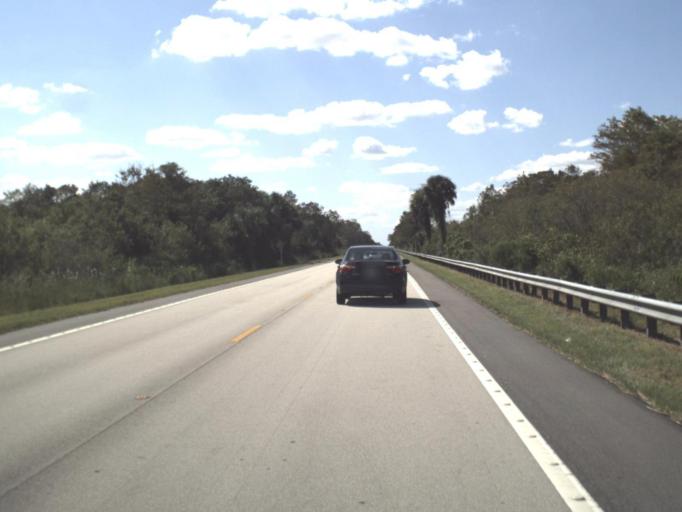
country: US
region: Florida
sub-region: Miami-Dade County
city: Kendall West
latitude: 25.8601
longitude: -81.0653
